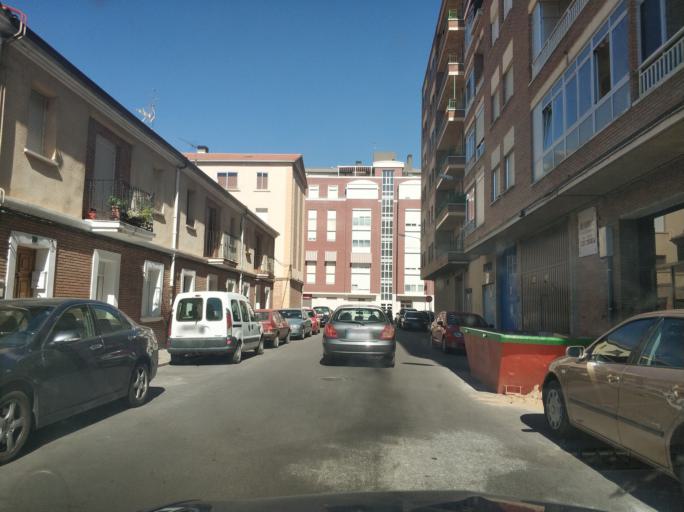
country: ES
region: Castille and Leon
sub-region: Provincia de Burgos
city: Aranda de Duero
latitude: 41.6722
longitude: -3.6773
